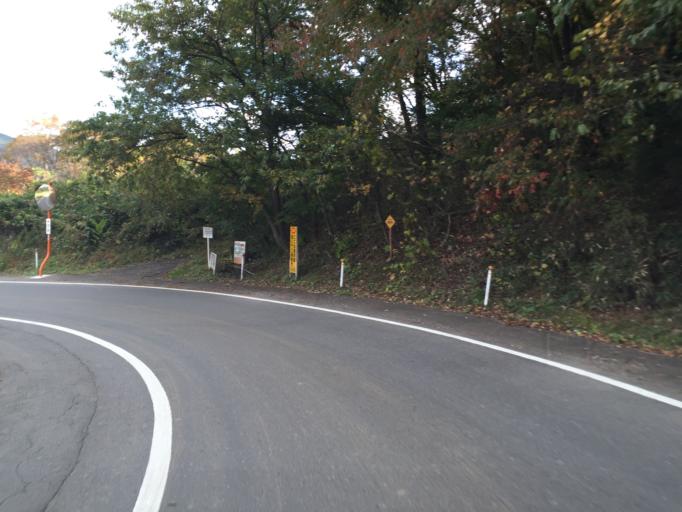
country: JP
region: Fukushima
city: Fukushima-shi
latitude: 37.7121
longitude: 140.3455
